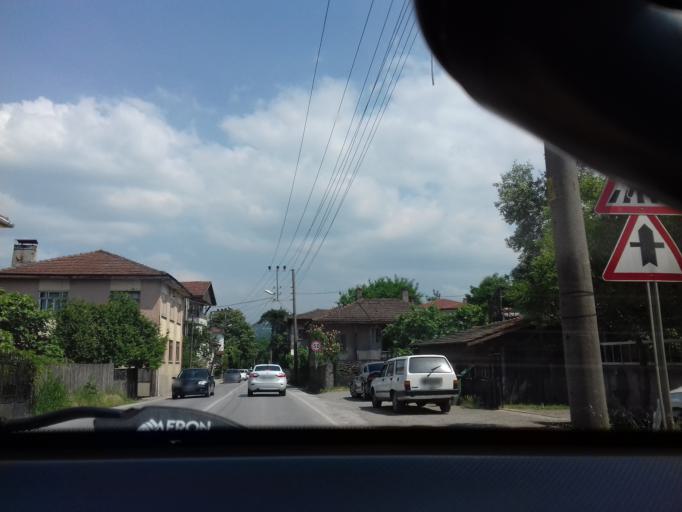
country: TR
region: Sakarya
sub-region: Merkez
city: Sapanca
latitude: 40.6890
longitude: 30.2636
